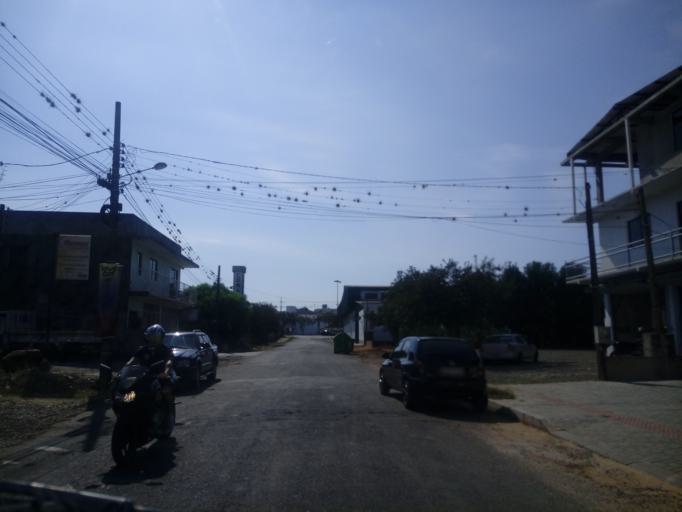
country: BR
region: Santa Catarina
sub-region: Chapeco
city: Chapeco
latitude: -27.0805
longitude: -52.6248
